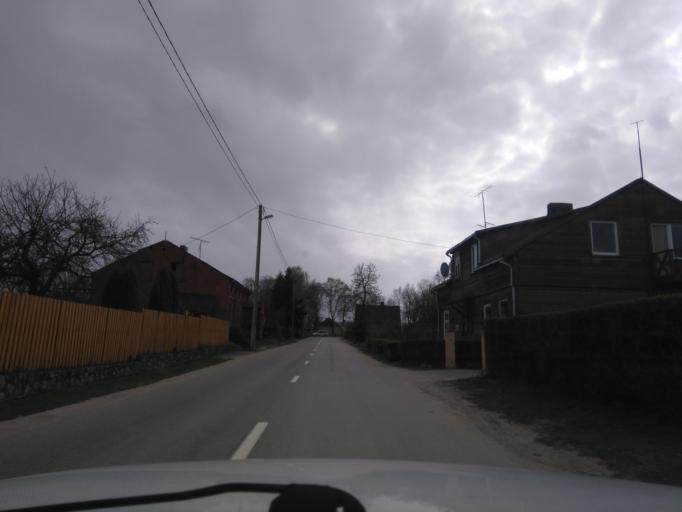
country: LT
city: Virbalis
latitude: 54.6280
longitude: 22.8237
